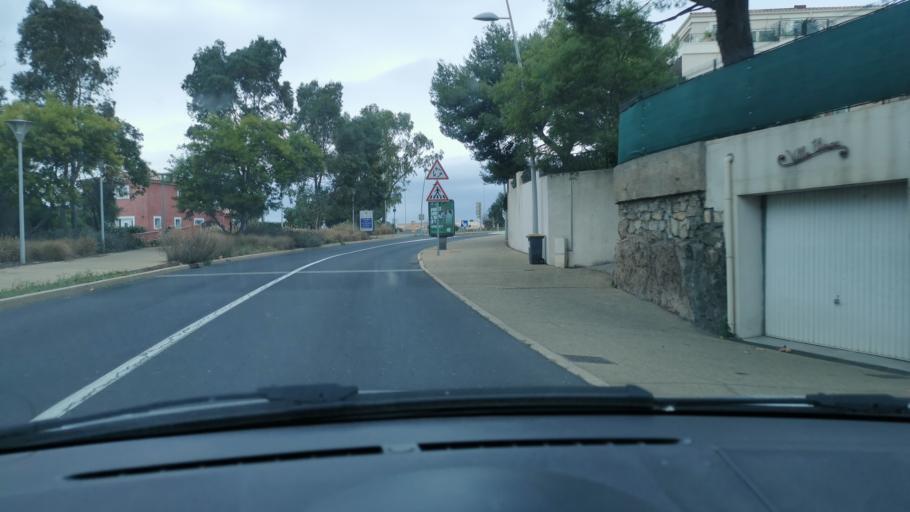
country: FR
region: Languedoc-Roussillon
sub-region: Departement de l'Herault
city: Sete
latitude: 43.4004
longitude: 3.6618
